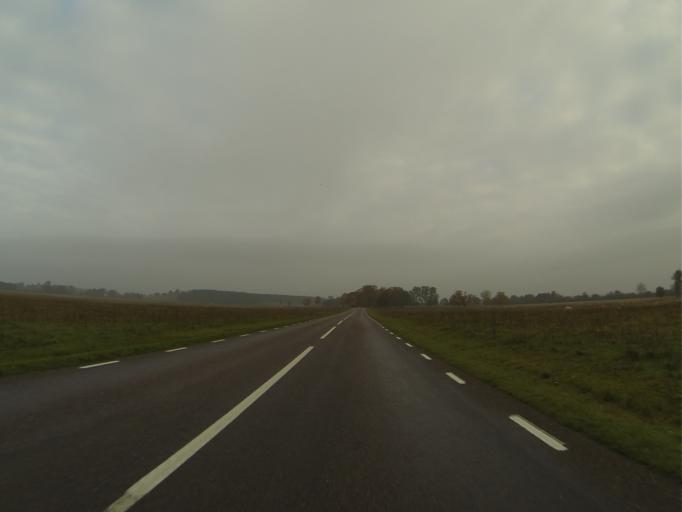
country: SE
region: Skane
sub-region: Lunds Kommun
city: Veberod
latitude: 55.6730
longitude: 13.4953
